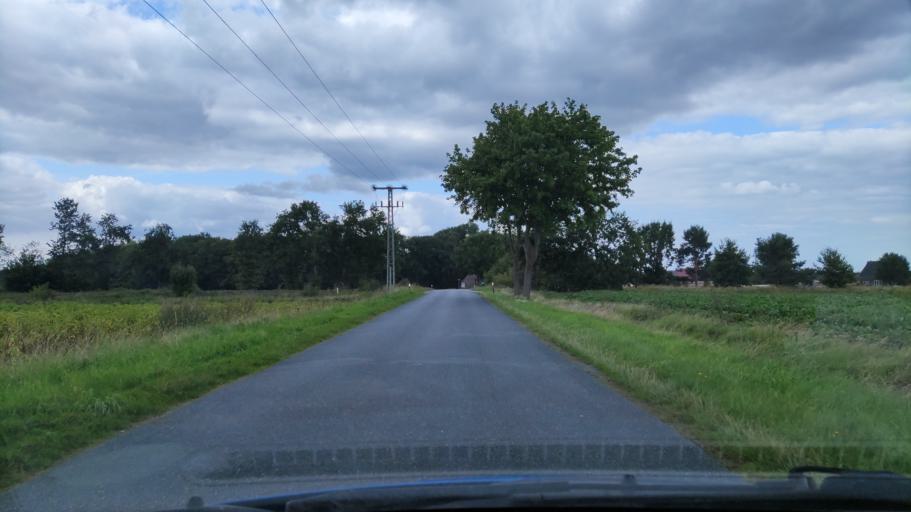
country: DE
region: Lower Saxony
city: Weste
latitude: 53.0564
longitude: 10.7092
